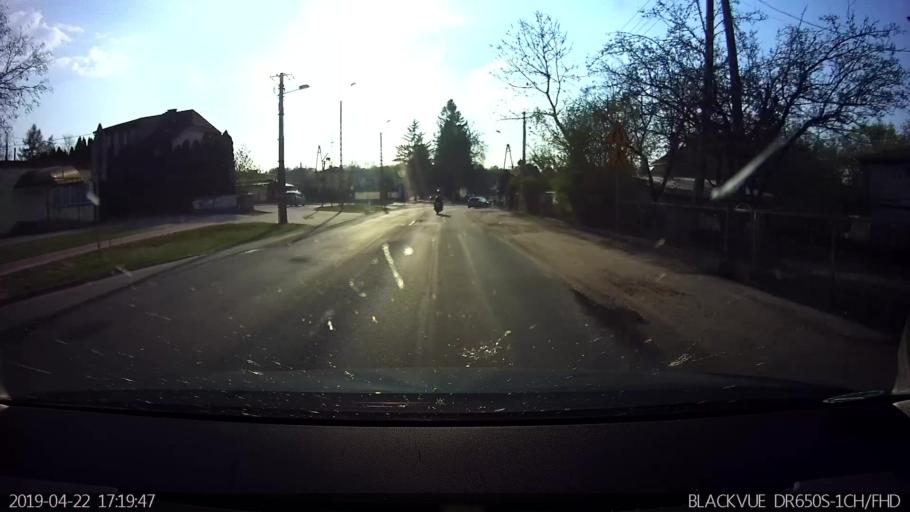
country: PL
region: Masovian Voivodeship
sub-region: Powiat sokolowski
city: Repki
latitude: 52.3853
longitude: 22.3893
